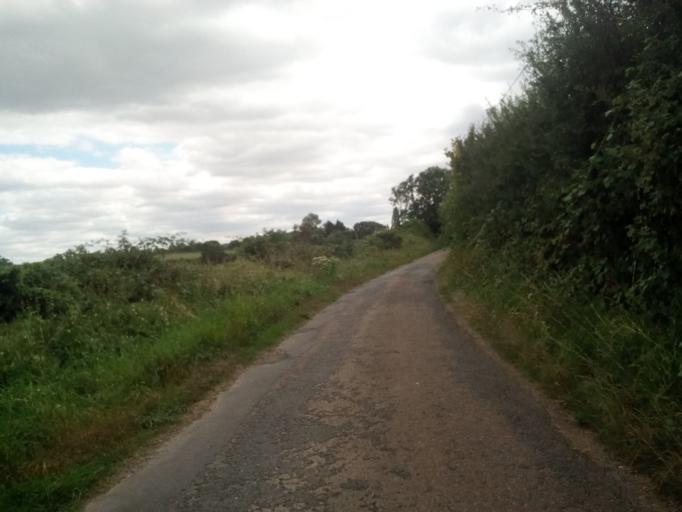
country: FR
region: Lower Normandy
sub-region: Departement du Calvados
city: Troarn
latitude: 49.1621
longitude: -0.1534
